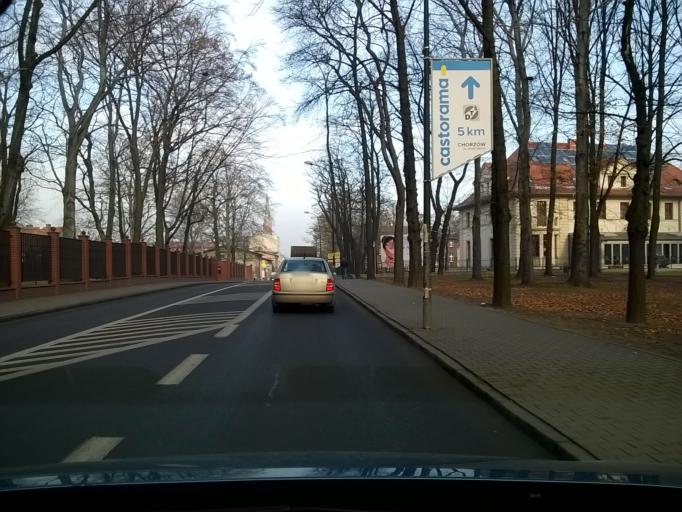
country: PL
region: Silesian Voivodeship
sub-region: Swietochlowice
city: Swietochlowice
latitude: 50.2696
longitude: 18.9377
